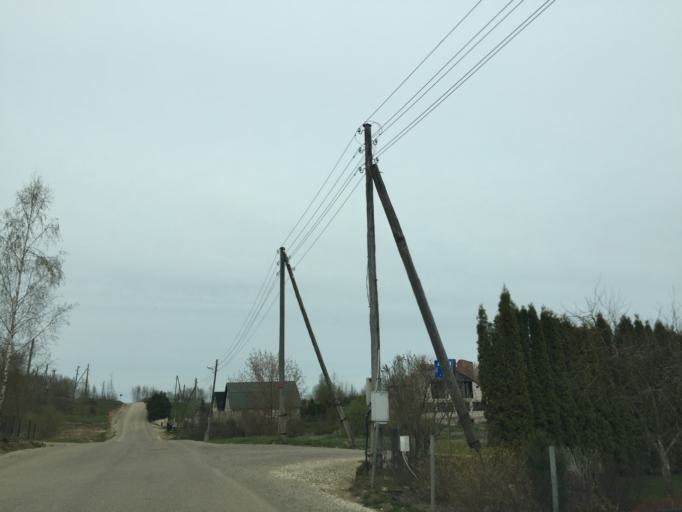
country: LV
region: Ludzas Rajons
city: Ludza
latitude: 56.5505
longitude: 27.6975
